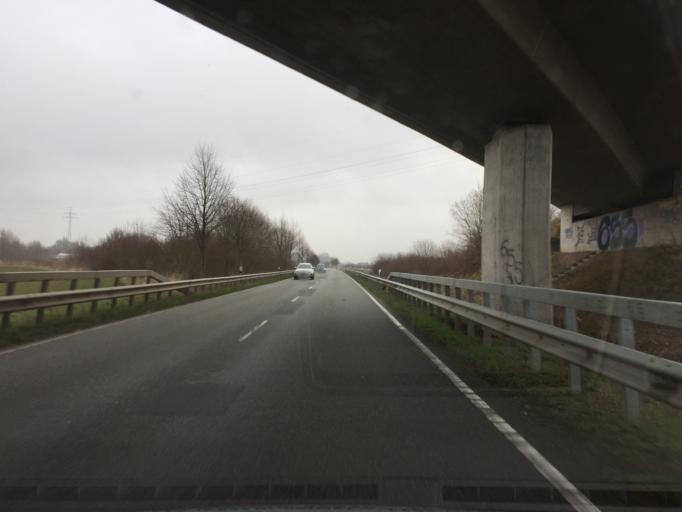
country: DE
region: North Rhine-Westphalia
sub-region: Regierungsbezirk Detmold
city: Petershagen
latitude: 52.3736
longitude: 9.0240
